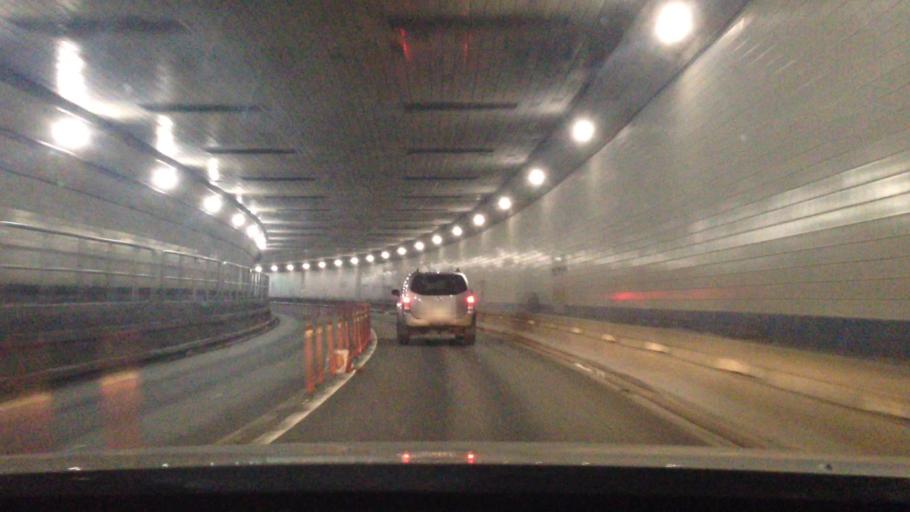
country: US
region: New Jersey
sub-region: Hudson County
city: Weehawken
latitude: 40.7656
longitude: -74.0206
